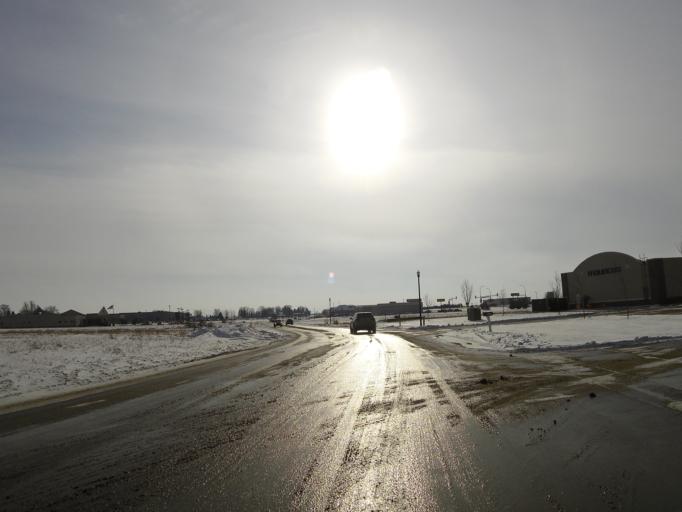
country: US
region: Minnesota
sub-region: McLeod County
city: Hutchinson
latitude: 44.8697
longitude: -94.3738
